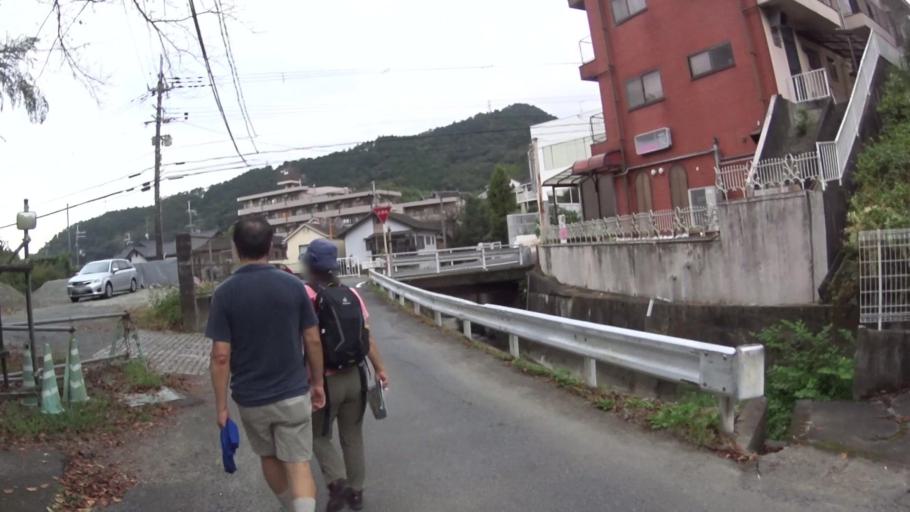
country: JP
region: Osaka
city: Kaizuka
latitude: 34.4571
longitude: 135.2897
